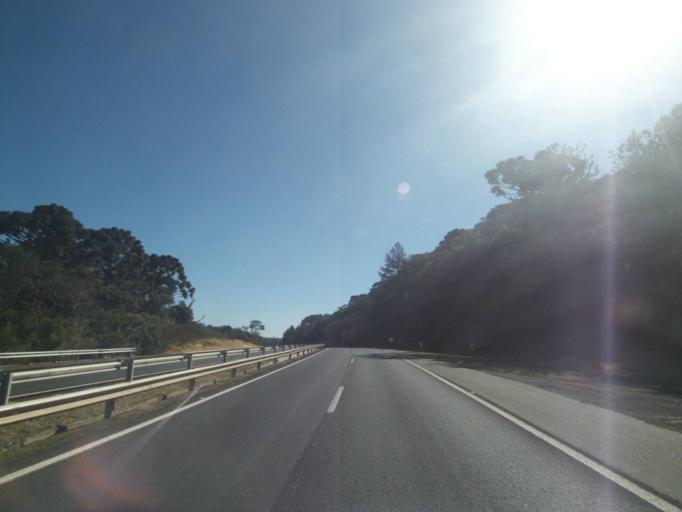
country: BR
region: Parana
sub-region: Tibagi
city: Tibagi
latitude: -24.7582
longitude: -50.5308
